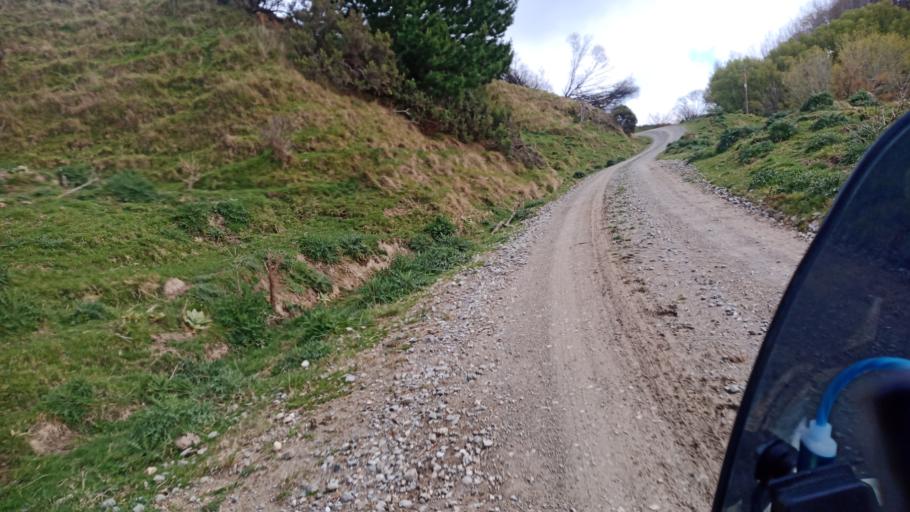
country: NZ
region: Gisborne
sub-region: Gisborne District
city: Gisborne
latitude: -38.5539
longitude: 178.1484
